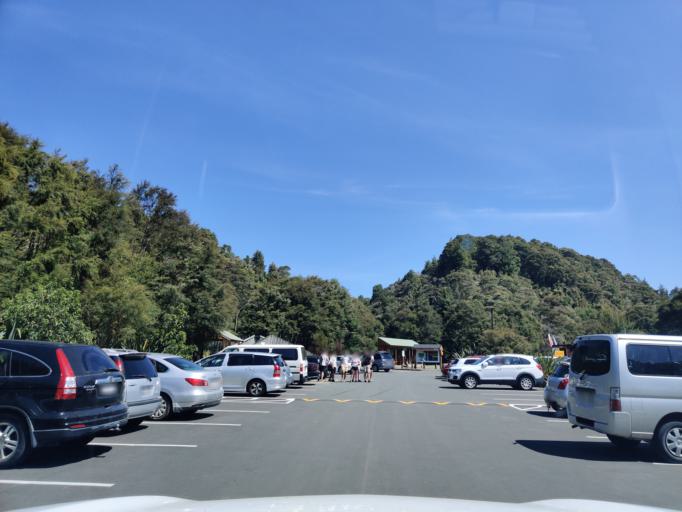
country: NZ
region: Auckland
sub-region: Auckland
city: Red Hill
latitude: -37.0663
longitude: 175.0894
